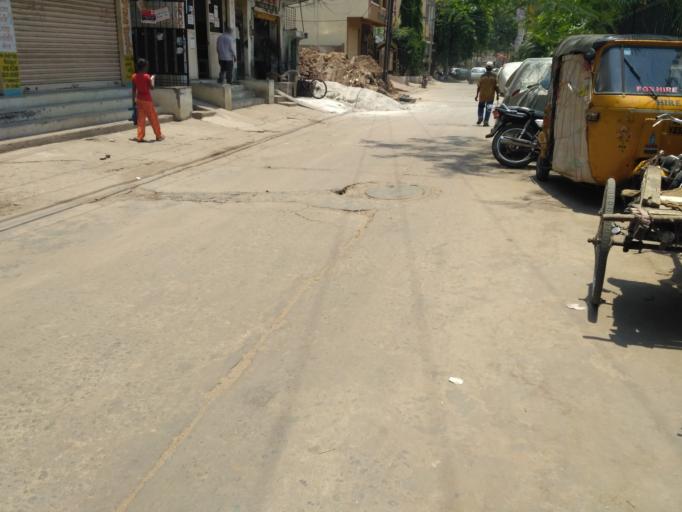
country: IN
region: Telangana
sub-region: Rangareddi
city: Quthbullapur
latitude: 17.4578
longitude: 78.4510
